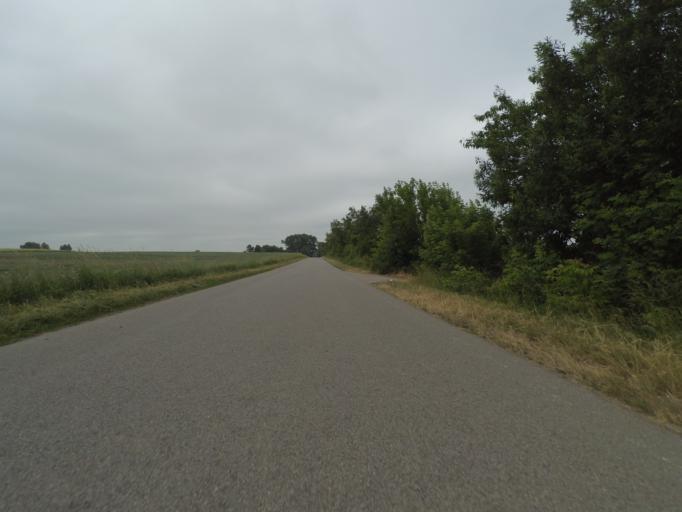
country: DE
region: Mecklenburg-Vorpommern
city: Goldberg
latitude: 53.5526
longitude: 12.0745
